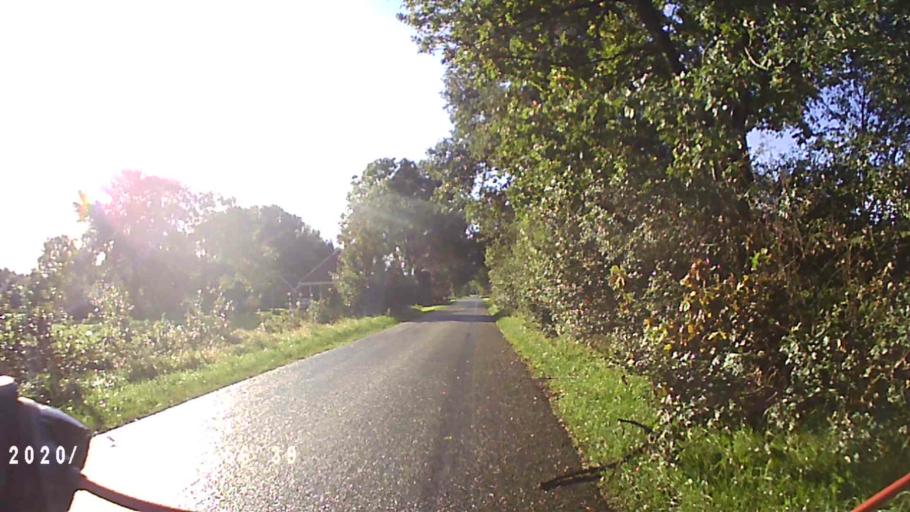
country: NL
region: Friesland
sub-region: Gemeente Achtkarspelen
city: Surhuisterveen
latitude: 53.1508
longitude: 6.2065
